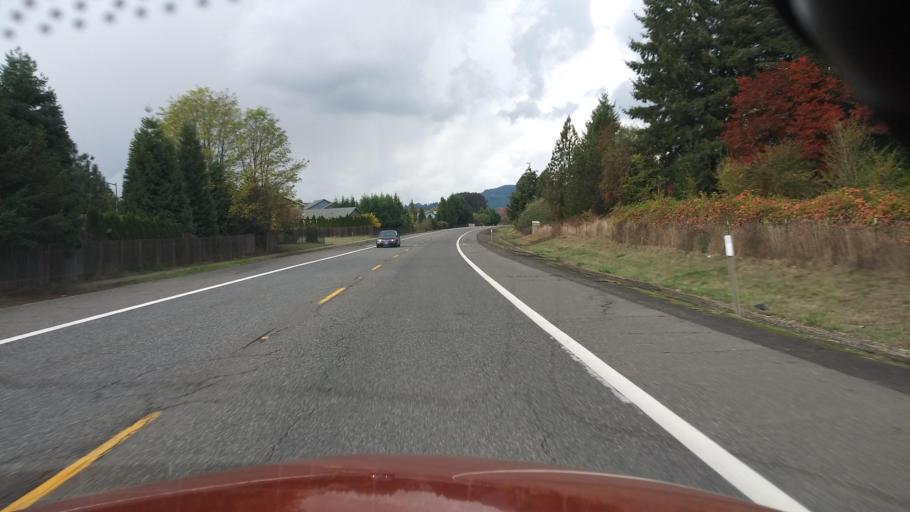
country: US
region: Oregon
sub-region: Washington County
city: Forest Grove
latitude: 45.5306
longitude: -123.0974
